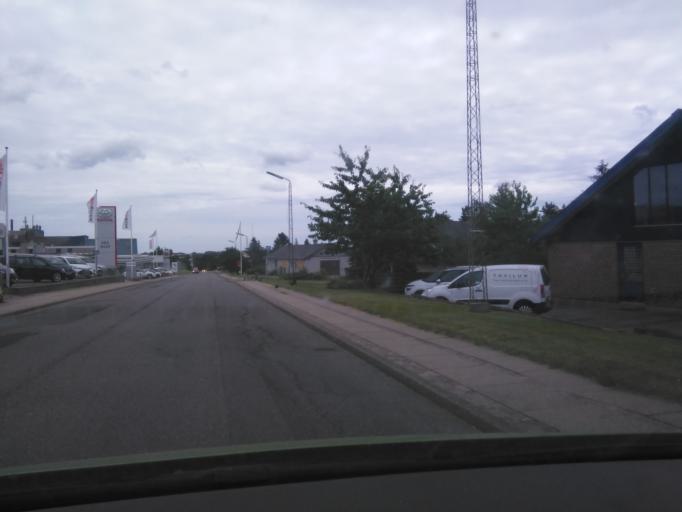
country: DK
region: Central Jutland
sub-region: Odder Kommune
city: Odder
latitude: 55.9854
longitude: 10.1432
